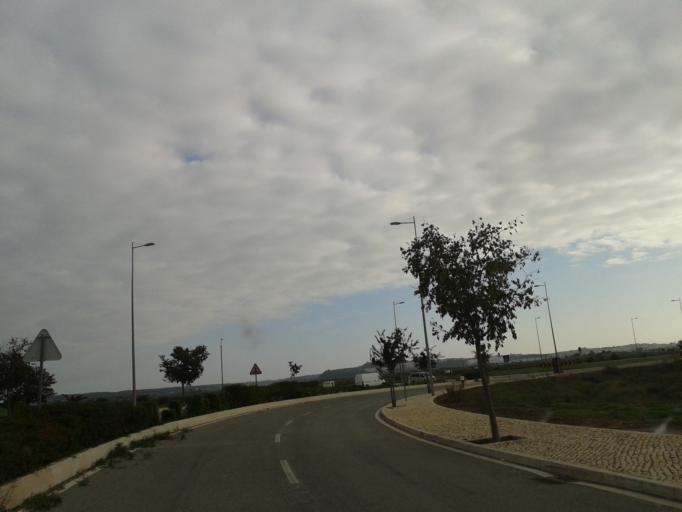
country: PT
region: Faro
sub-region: Castro Marim
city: Castro Marim
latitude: 37.2210
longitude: -7.4460
